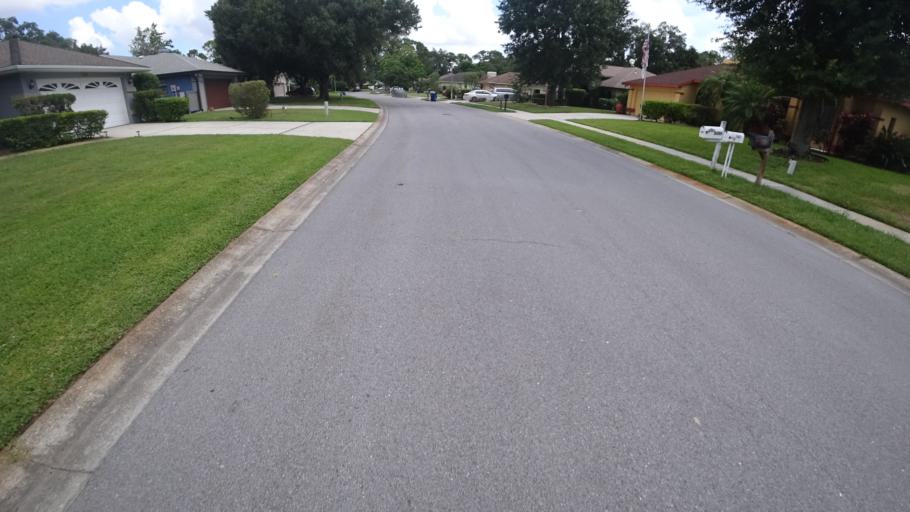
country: US
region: Florida
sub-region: Manatee County
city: Samoset
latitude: 27.4518
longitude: -82.5278
